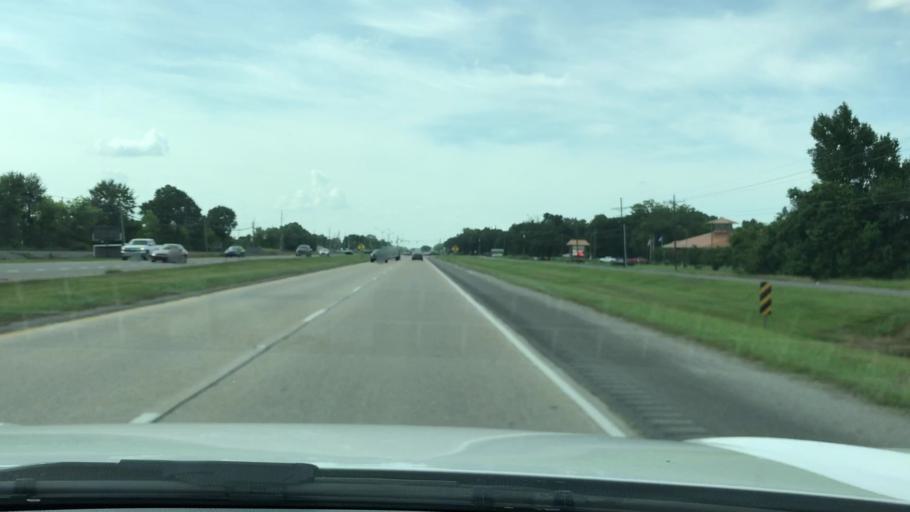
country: US
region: Louisiana
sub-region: Iberville Parish
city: Plaquemine
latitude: 30.3102
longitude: -91.2470
